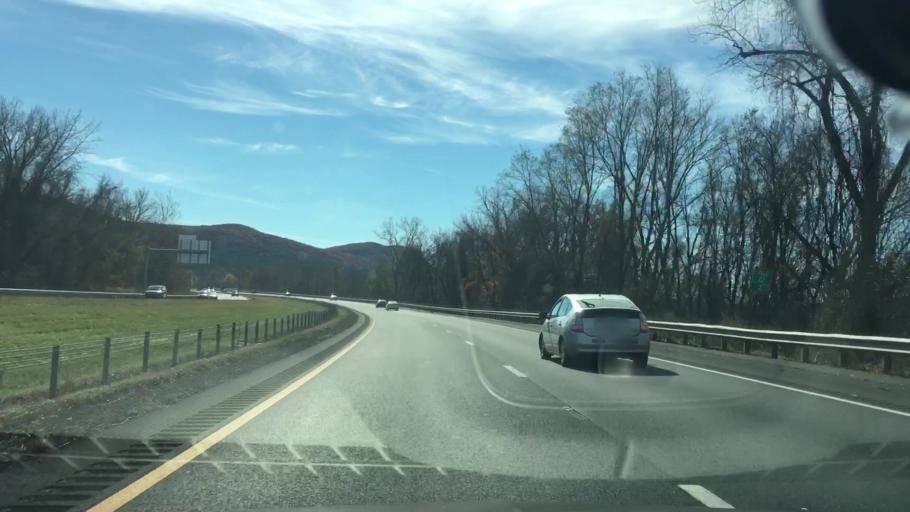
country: US
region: Massachusetts
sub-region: Hampshire County
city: Northampton
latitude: 42.3000
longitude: -72.6295
